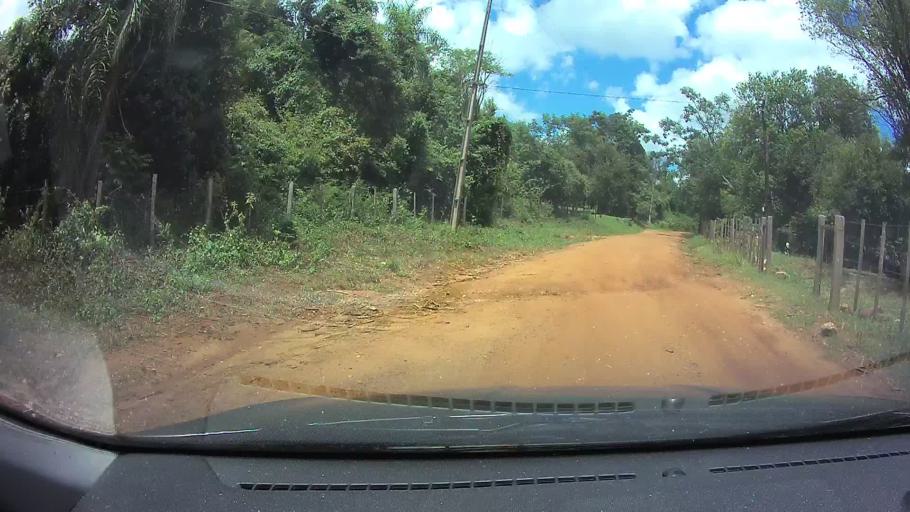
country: PY
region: Paraguari
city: La Colmena
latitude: -25.9334
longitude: -56.7838
